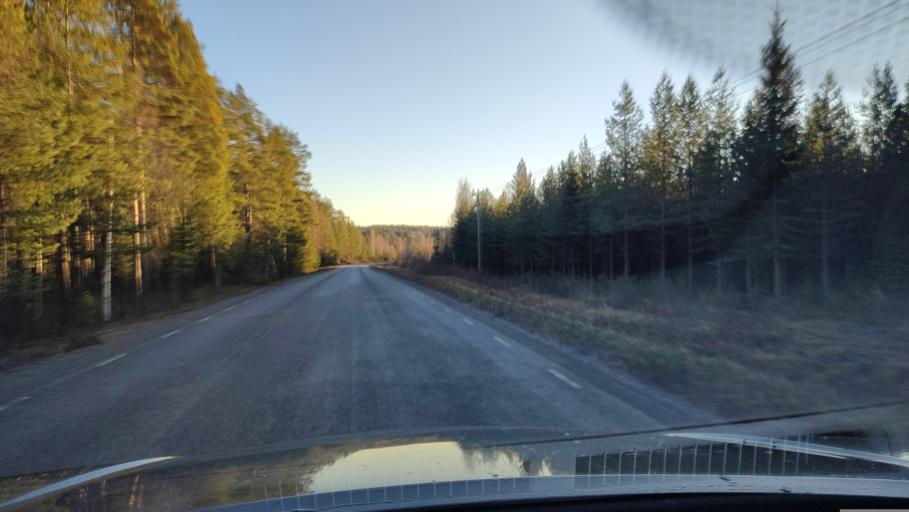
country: SE
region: Vaesterbotten
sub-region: Skelleftea Kommun
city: Viken
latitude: 64.6944
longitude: 20.9322
